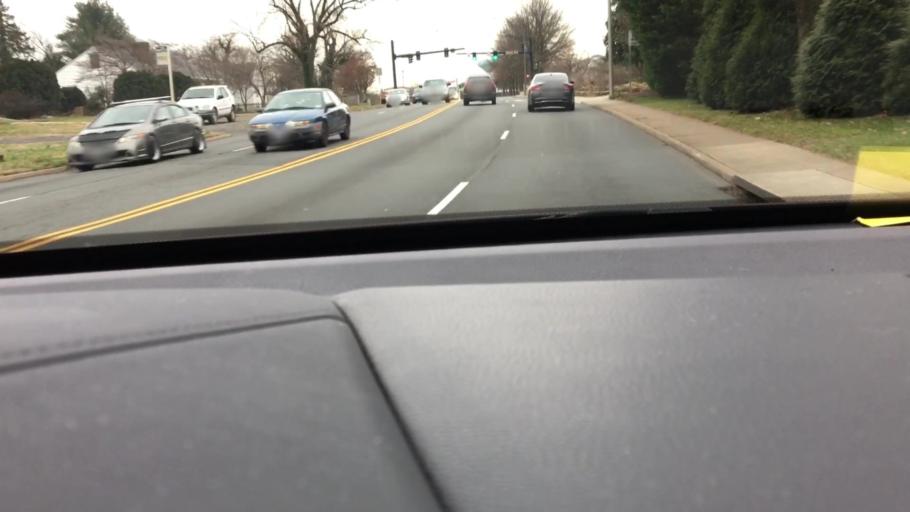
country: US
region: Virginia
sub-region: City of Manassas
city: Manassas
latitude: 38.7575
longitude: -77.4705
